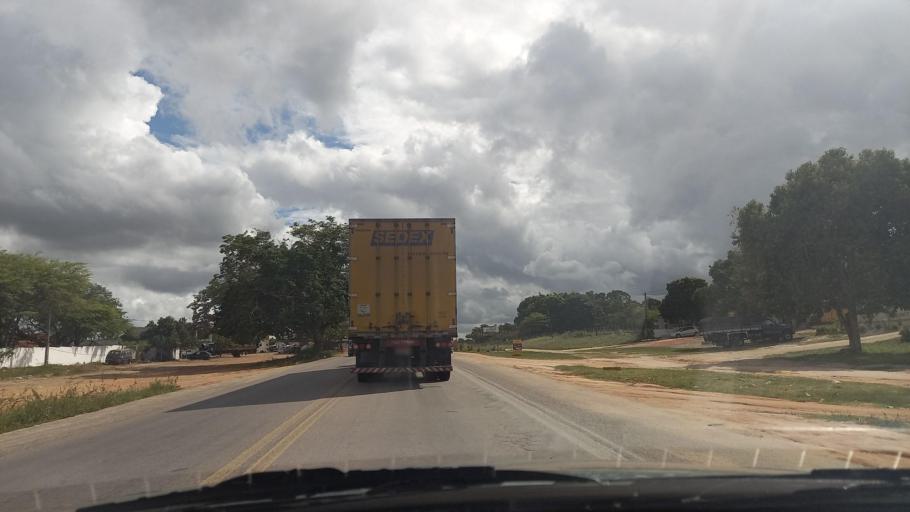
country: BR
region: Pernambuco
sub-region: Lajedo
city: Lajedo
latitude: -8.6577
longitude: -36.3271
